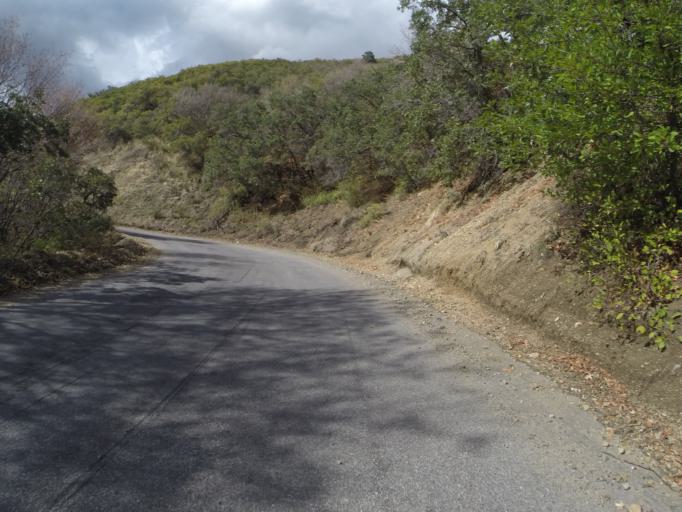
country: US
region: Utah
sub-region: Salt Lake County
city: Herriman
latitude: 40.4880
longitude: -112.1654
